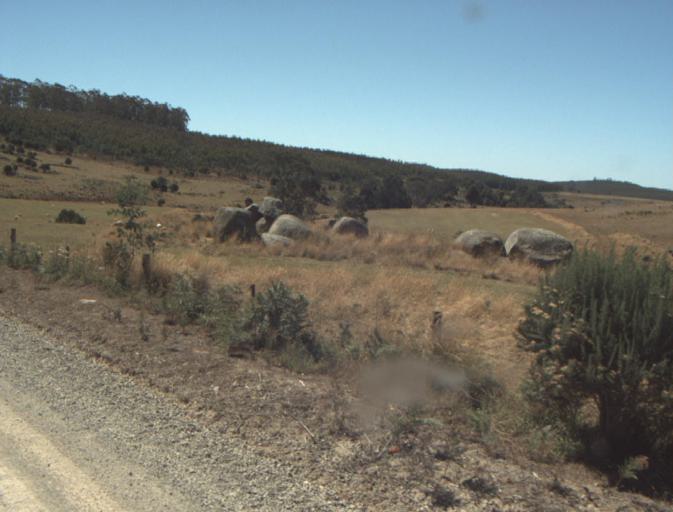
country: AU
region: Tasmania
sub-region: Dorset
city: Scottsdale
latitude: -41.3449
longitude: 147.4374
